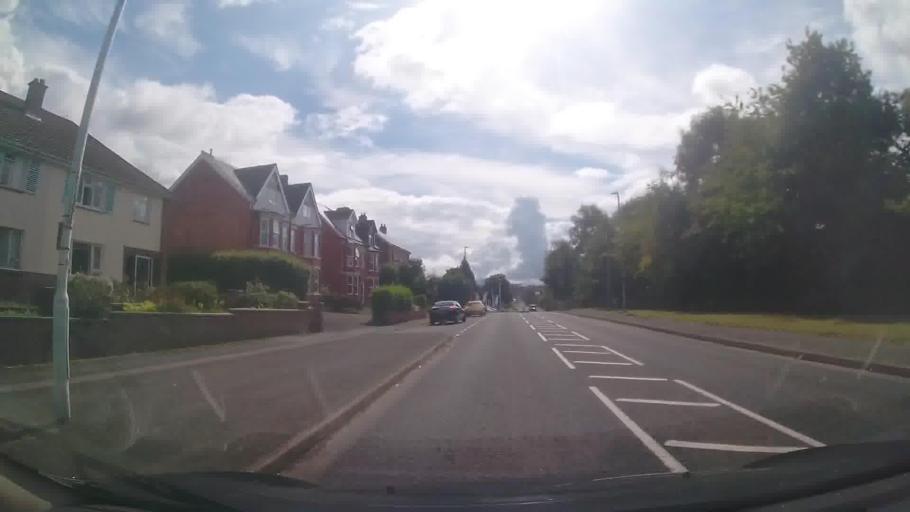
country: GB
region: Wales
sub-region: Sir Powys
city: Llandrindod Wells
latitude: 52.2463
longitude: -3.3767
